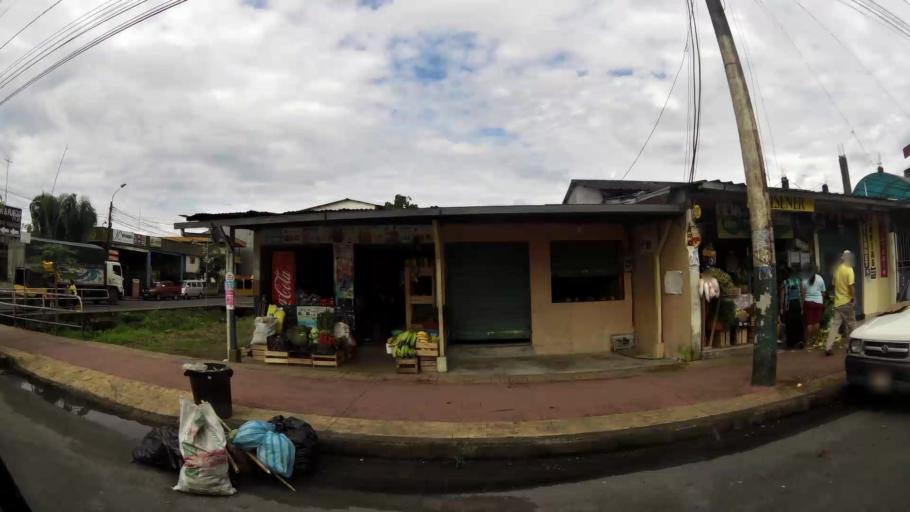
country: EC
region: Pastaza
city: Puyo
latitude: -1.4804
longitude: -78.0002
